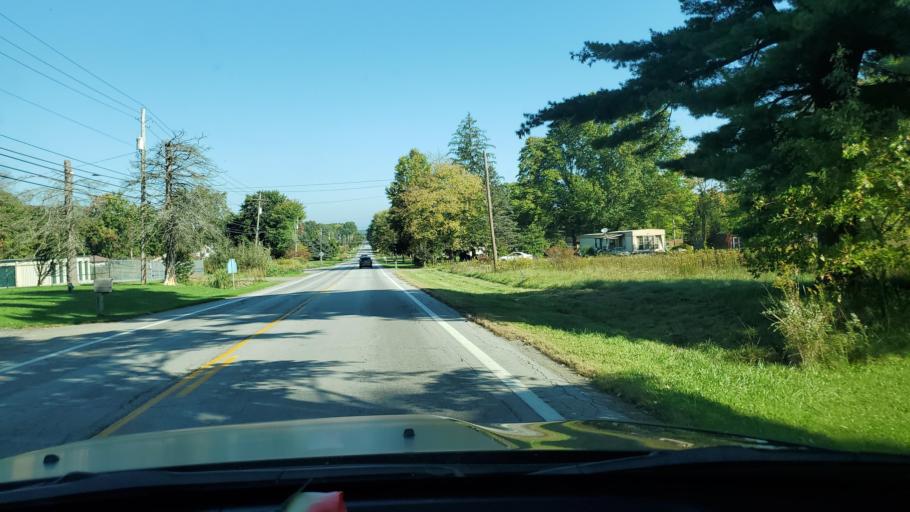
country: US
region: Ohio
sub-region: Trumbull County
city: Brookfield Center
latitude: 41.2455
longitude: -80.5682
